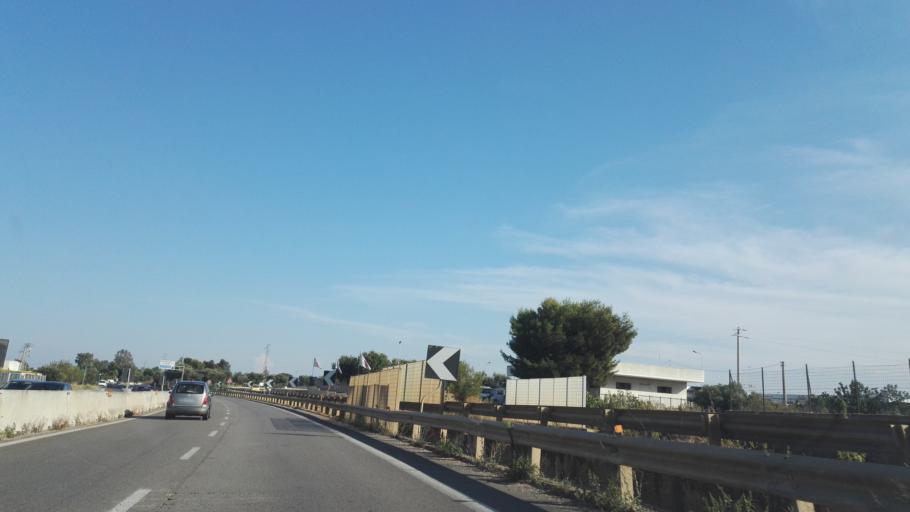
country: IT
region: Apulia
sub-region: Provincia di Bari
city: Polignano a Mare
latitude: 40.9900
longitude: 17.2081
